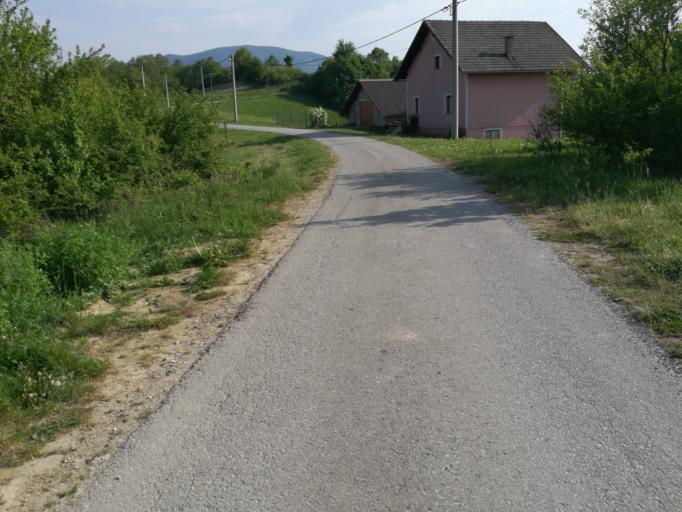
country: HR
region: Krapinsko-Zagorska
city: Radoboj
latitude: 46.2385
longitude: 15.9091
